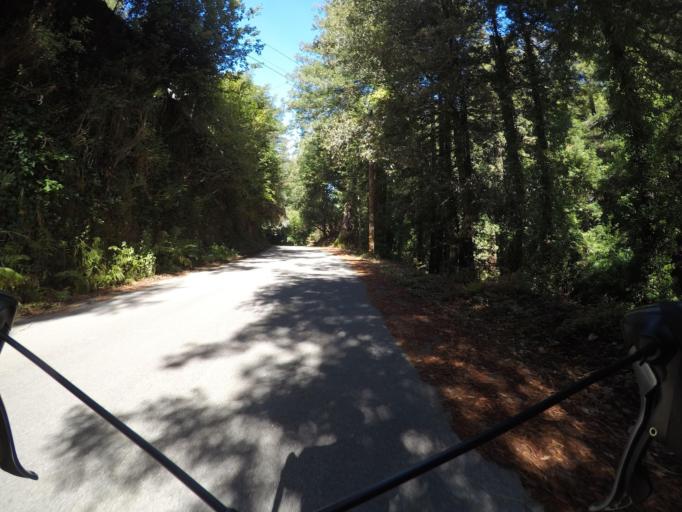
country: US
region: California
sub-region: Santa Cruz County
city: Scotts Valley
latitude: 37.0330
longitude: -122.0090
